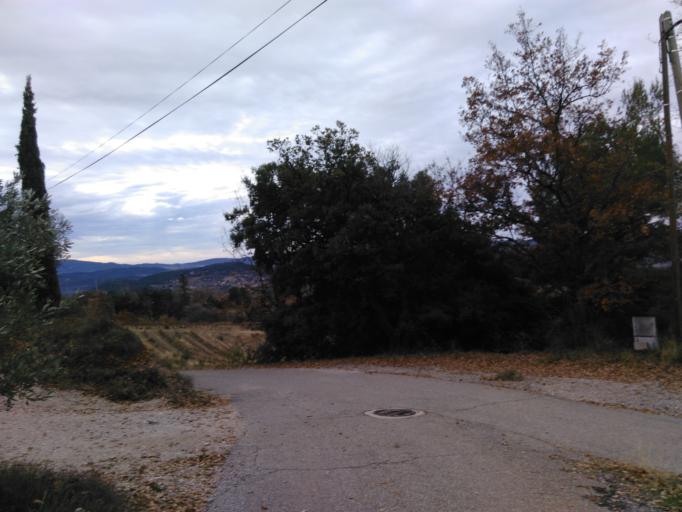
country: FR
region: Rhone-Alpes
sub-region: Departement de la Drome
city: Mirabel-aux-Baronnies
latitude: 44.2865
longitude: 5.1569
